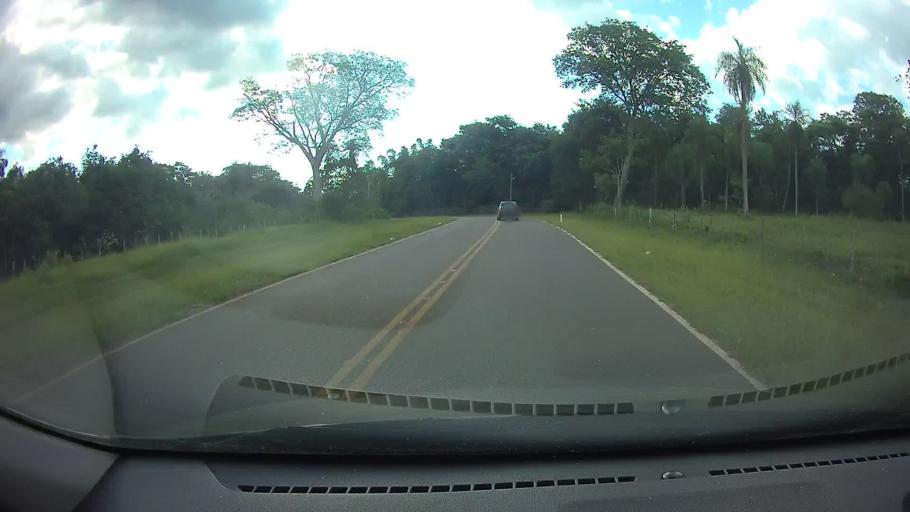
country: PY
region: Cordillera
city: Atyra
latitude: -25.2843
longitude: -57.1979
